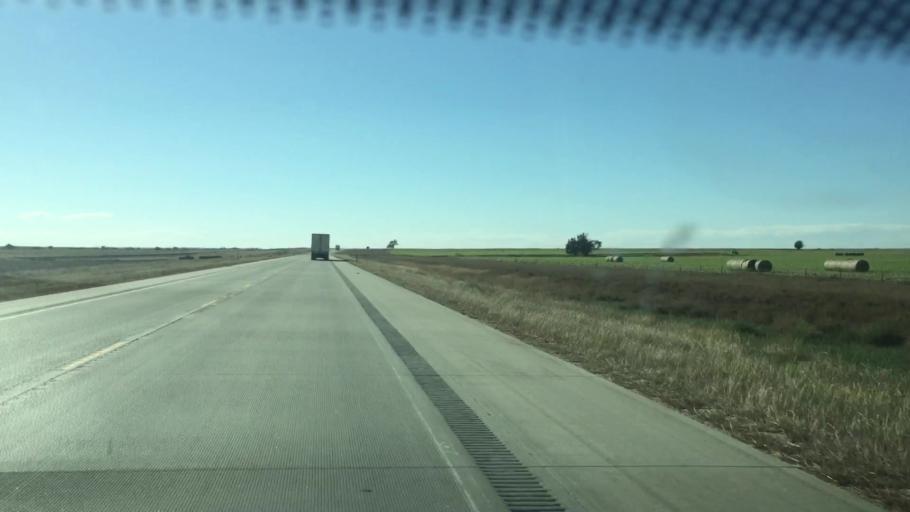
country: US
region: Colorado
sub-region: Kiowa County
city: Eads
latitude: 38.7639
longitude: -102.8140
